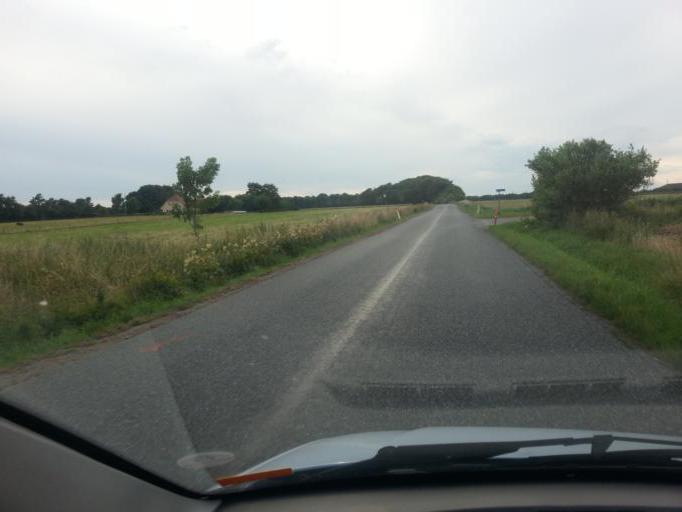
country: DK
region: South Denmark
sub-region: Vejen Kommune
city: Holsted
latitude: 55.4700
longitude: 8.8242
